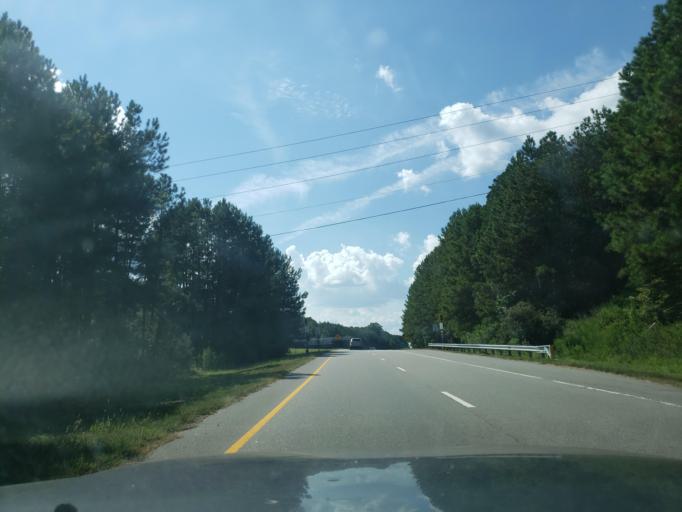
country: US
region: North Carolina
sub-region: Wake County
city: West Raleigh
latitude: 35.9155
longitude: -78.6839
